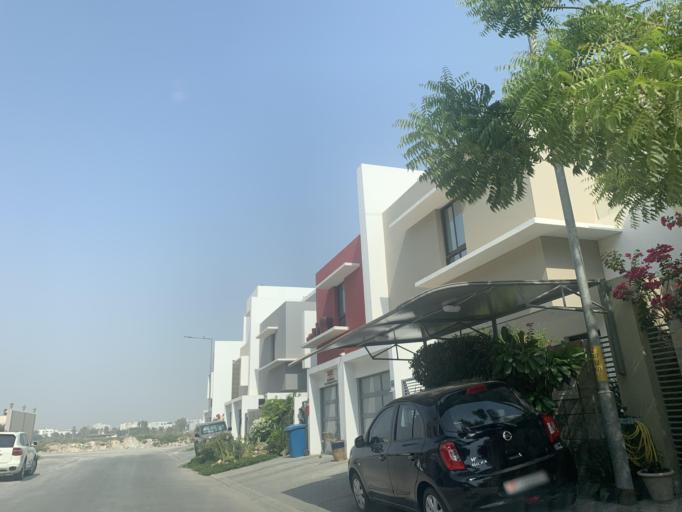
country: BH
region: Manama
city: Jidd Hafs
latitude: 26.2101
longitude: 50.4928
